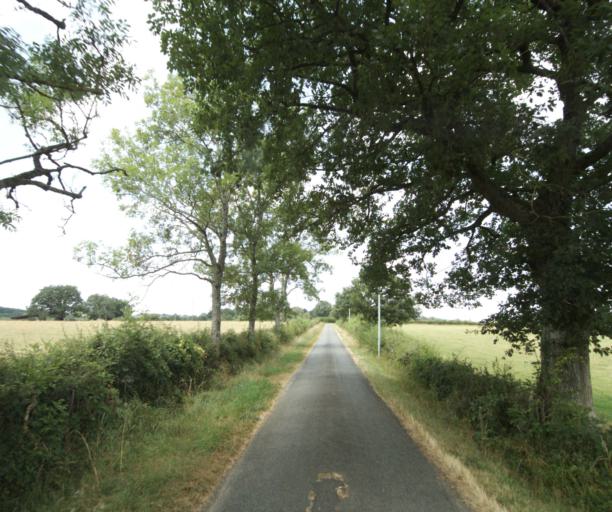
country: FR
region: Bourgogne
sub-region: Departement de Saone-et-Loire
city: Gueugnon
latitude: 46.5853
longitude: 4.0362
